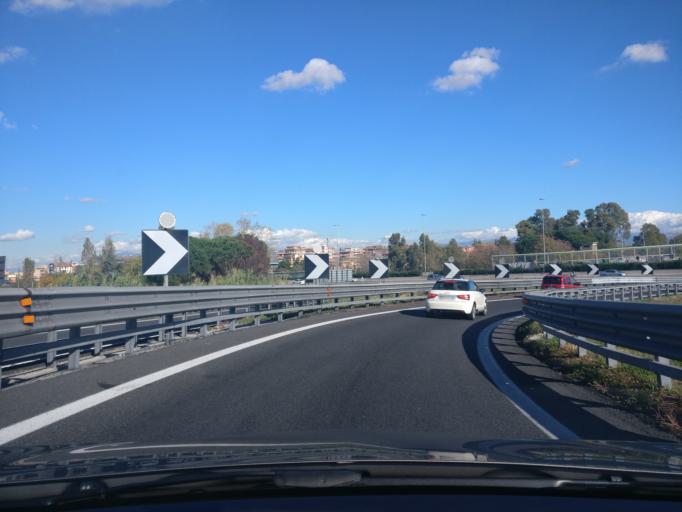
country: IT
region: Latium
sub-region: Citta metropolitana di Roma Capitale
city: Ciampino
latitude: 41.8545
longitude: 12.5965
